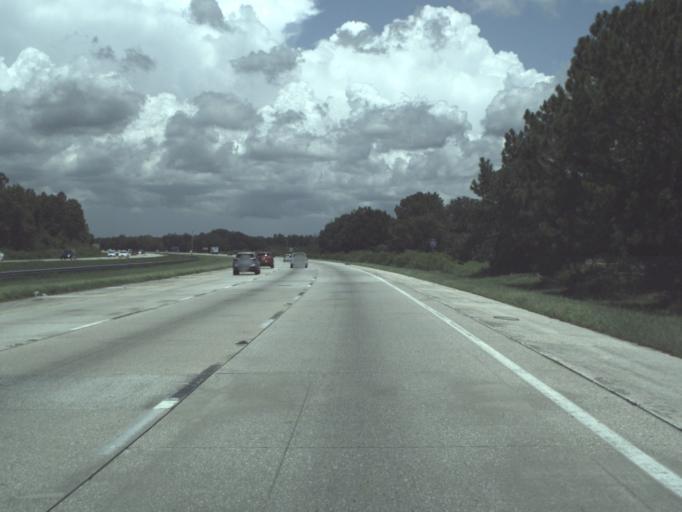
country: US
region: Florida
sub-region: Hillsborough County
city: Mango
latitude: 28.0125
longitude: -82.3282
